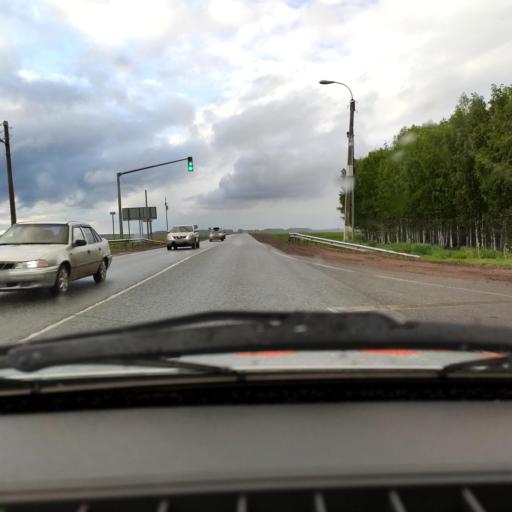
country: RU
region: Bashkortostan
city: Sterlitamak
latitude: 53.6580
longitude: 55.8484
